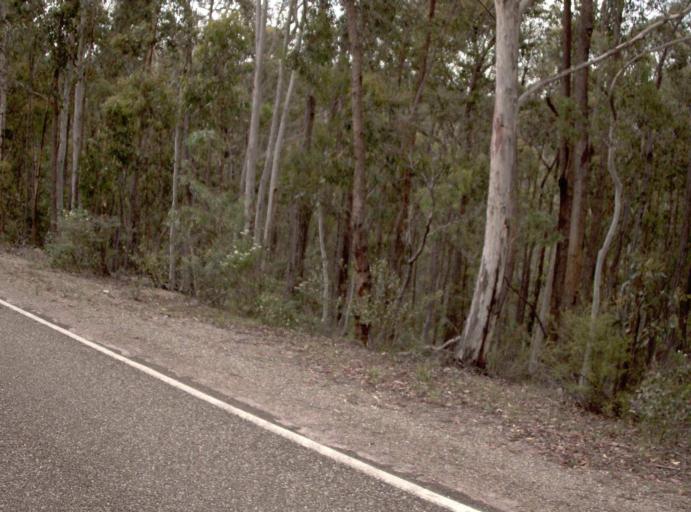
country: AU
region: Victoria
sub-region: East Gippsland
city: Bairnsdale
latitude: -37.6492
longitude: 147.2777
